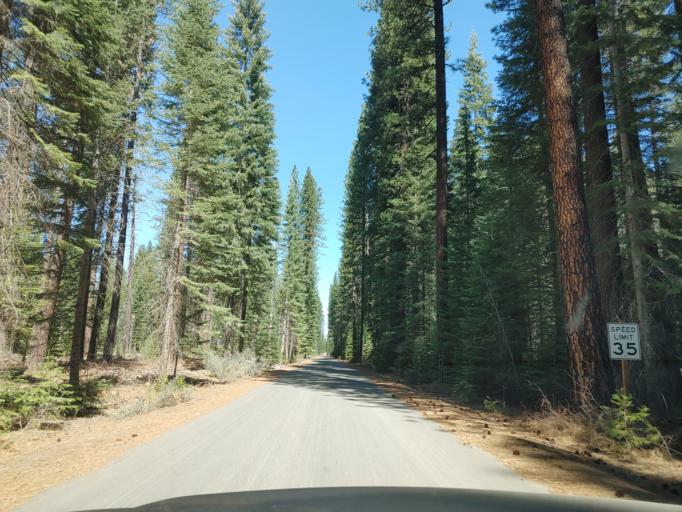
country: US
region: California
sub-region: Siskiyou County
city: McCloud
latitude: 41.2561
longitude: -121.9427
